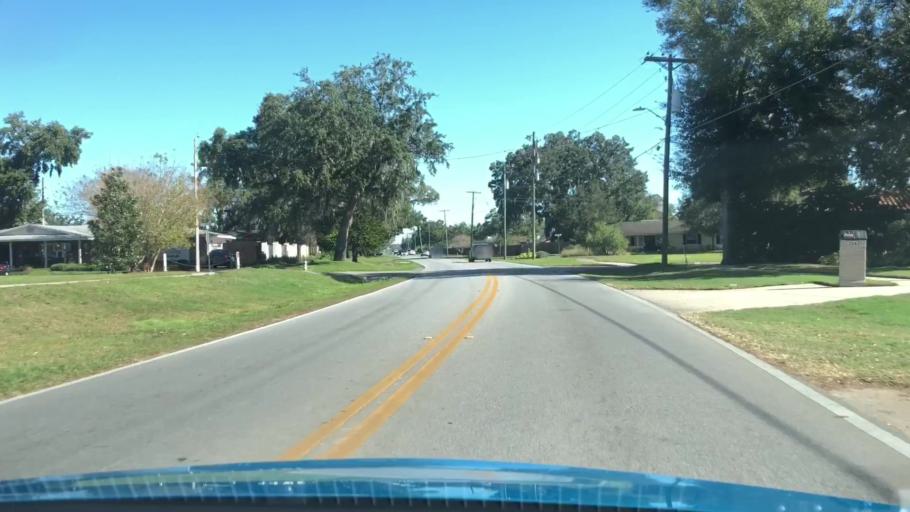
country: US
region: Florida
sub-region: Orange County
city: Pine Castle
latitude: 28.4805
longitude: -81.3444
